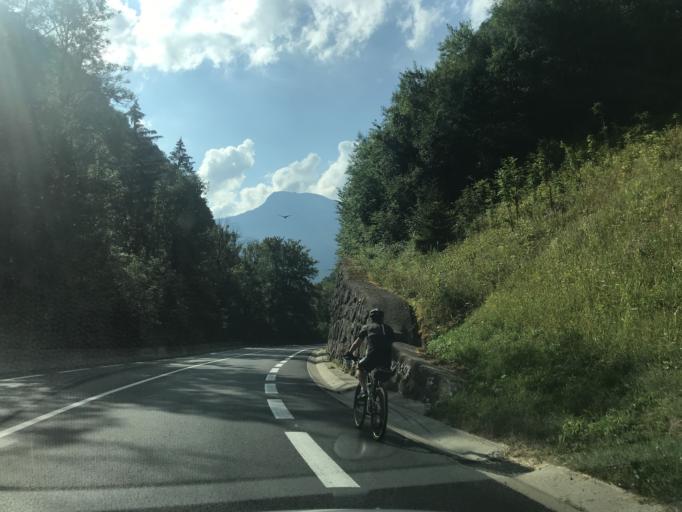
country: FR
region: Rhone-Alpes
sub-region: Departement de la Haute-Savoie
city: Dingy-Saint-Clair
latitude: 45.9077
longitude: 6.2024
